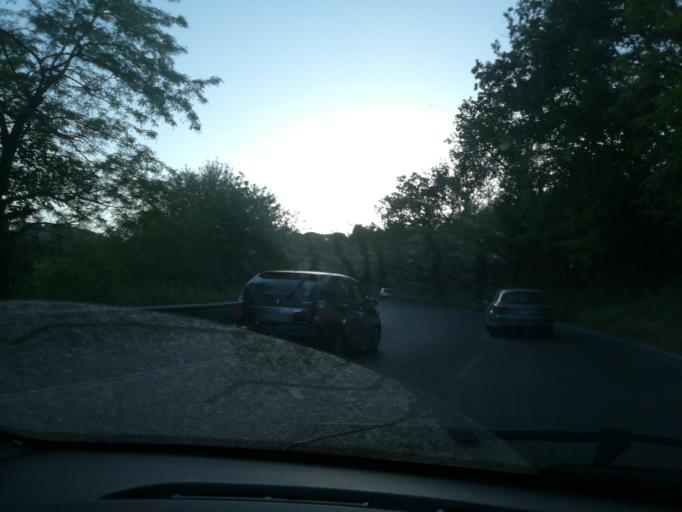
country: IT
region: The Marches
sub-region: Provincia di Macerata
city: Piediripa
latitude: 43.2855
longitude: 13.4768
